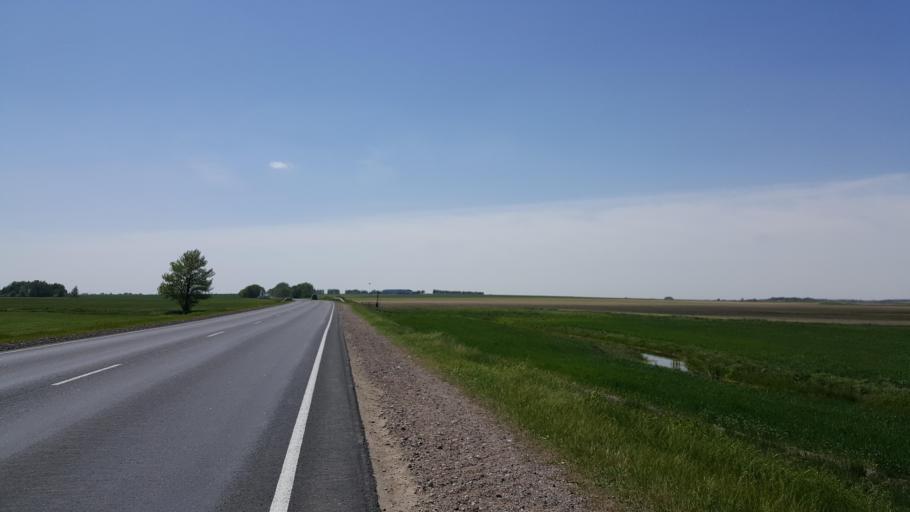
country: BY
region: Brest
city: Charnawchytsy
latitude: 52.2529
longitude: 23.7532
